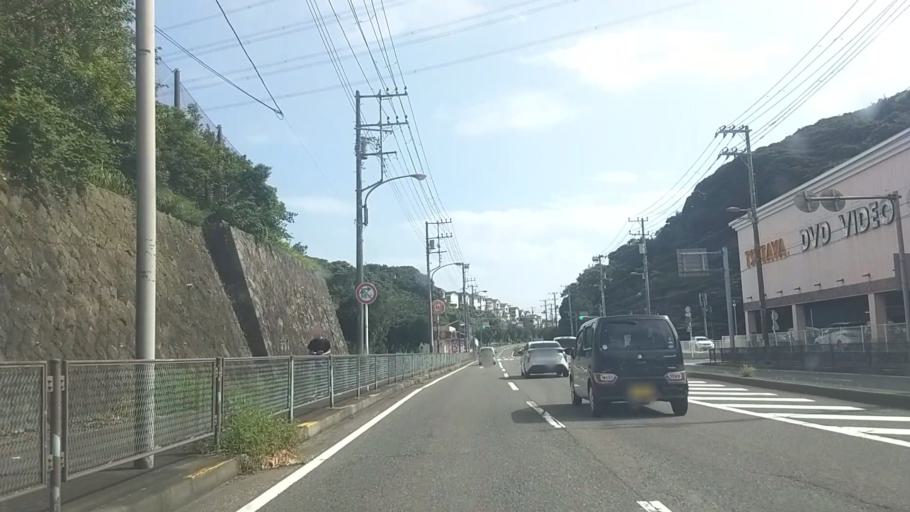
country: JP
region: Kanagawa
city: Yokosuka
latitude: 35.2241
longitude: 139.6845
